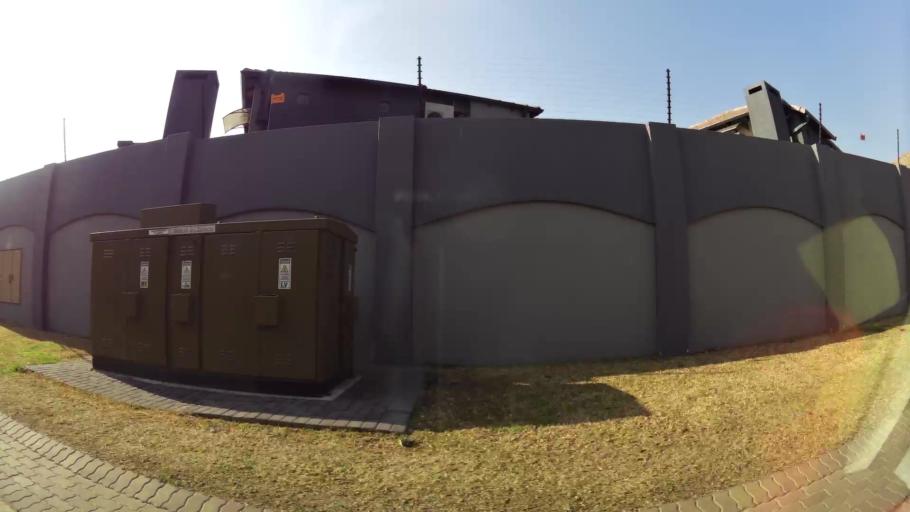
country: ZA
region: Gauteng
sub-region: City of Tshwane Metropolitan Municipality
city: Pretoria
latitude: -25.7565
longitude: 28.3369
